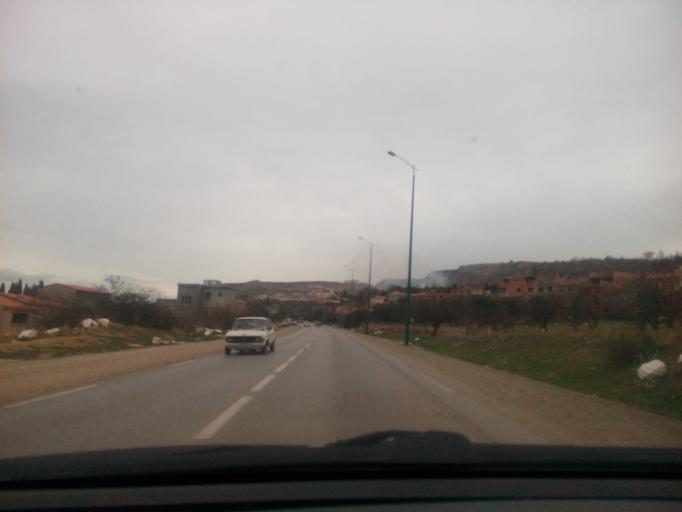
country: DZ
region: Tlemcen
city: Mansoura
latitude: 34.8637
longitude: -1.3388
